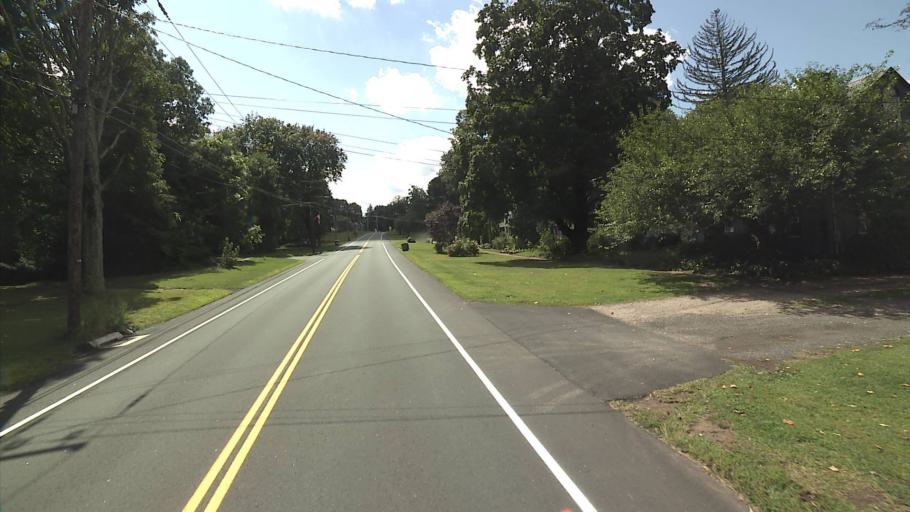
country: US
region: Connecticut
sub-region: Middlesex County
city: Cromwell
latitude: 41.5952
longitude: -72.6216
